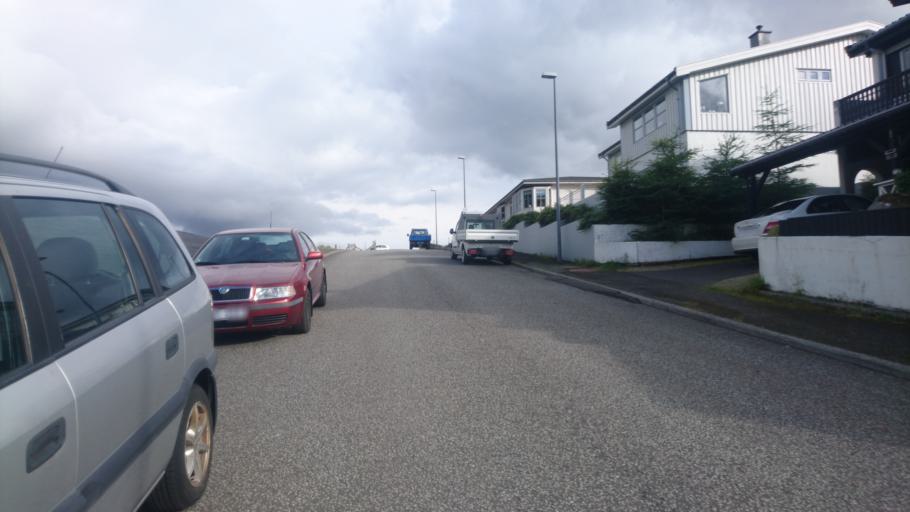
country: FO
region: Nordoyar
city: Klaksvik
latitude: 62.2198
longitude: -6.5786
